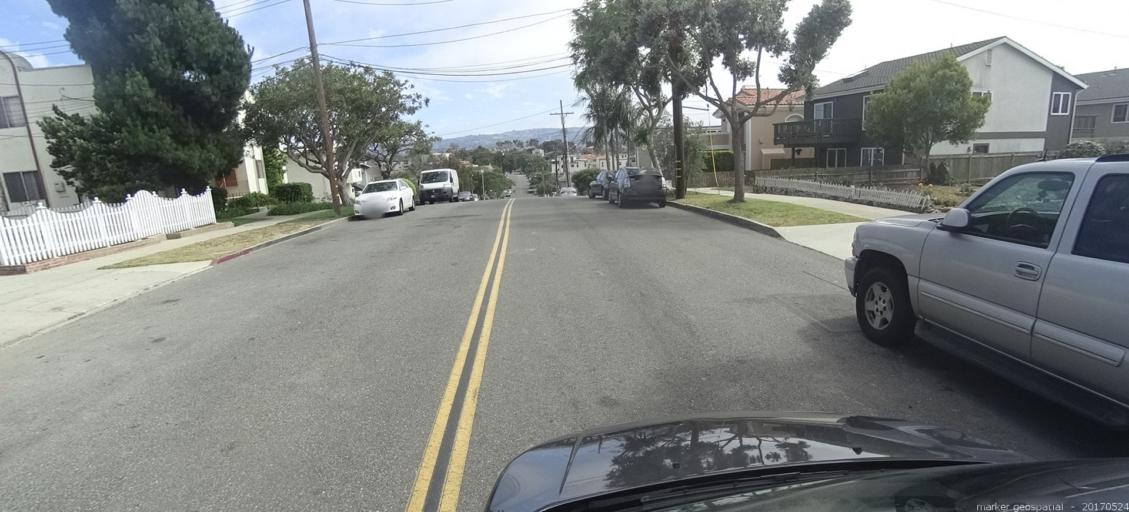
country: US
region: California
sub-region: Los Angeles County
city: Redondo Beach
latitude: 33.8398
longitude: -118.3777
